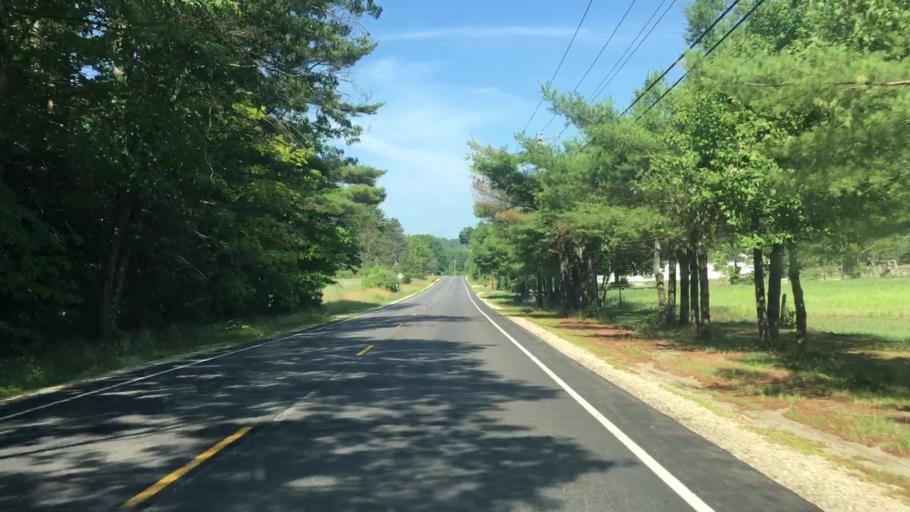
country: US
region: New Hampshire
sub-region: Merrimack County
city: Contoocook
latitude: 43.1936
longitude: -71.7302
